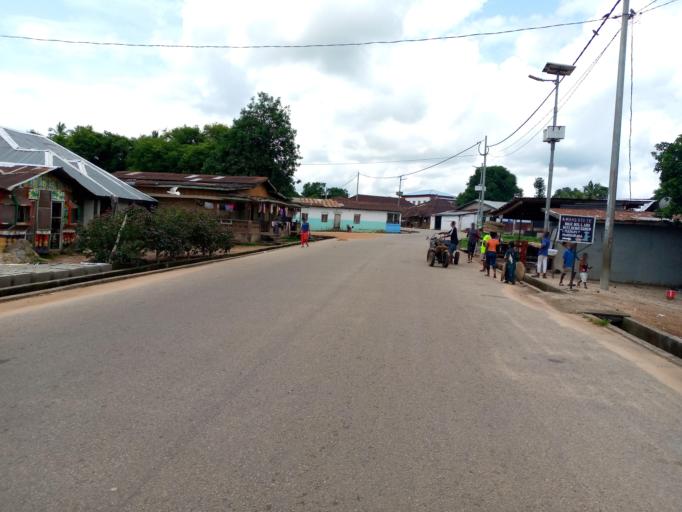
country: SL
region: Northern Province
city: Magburaka
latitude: 8.7212
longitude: -11.9551
